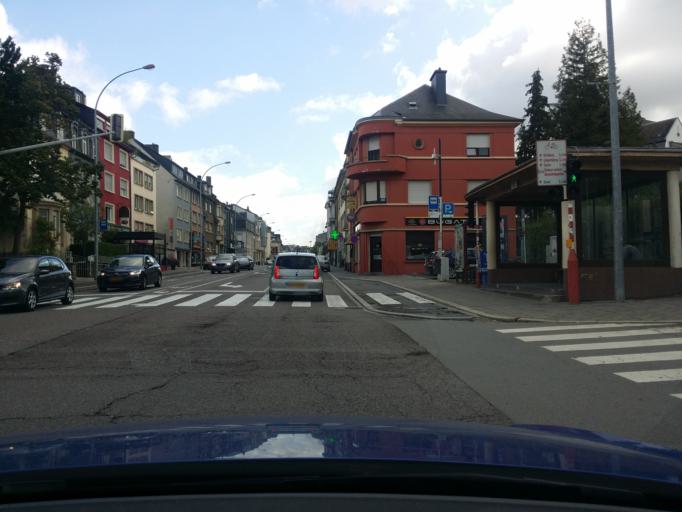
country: LU
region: Luxembourg
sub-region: Canton de Luxembourg
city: Luxembourg
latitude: 49.6063
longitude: 6.1064
